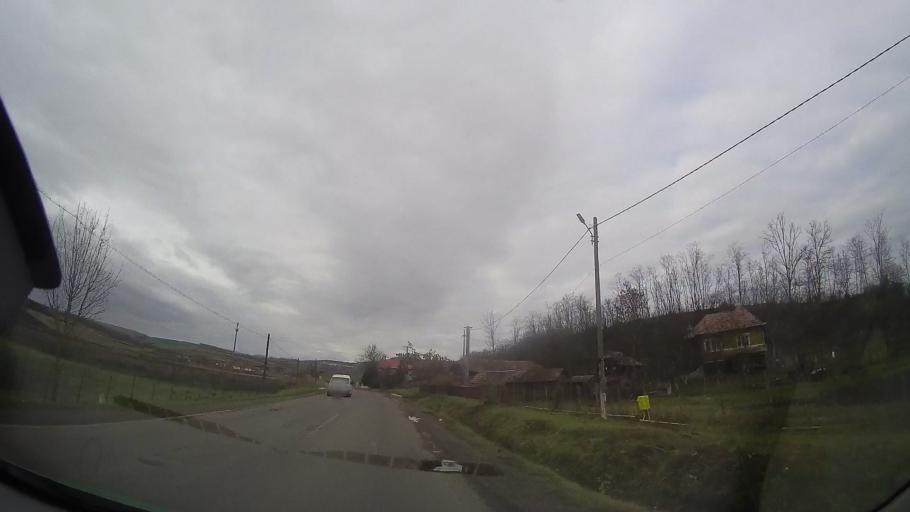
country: RO
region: Bistrita-Nasaud
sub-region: Comuna Urmenis
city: Urmenis
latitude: 46.7674
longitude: 24.3679
